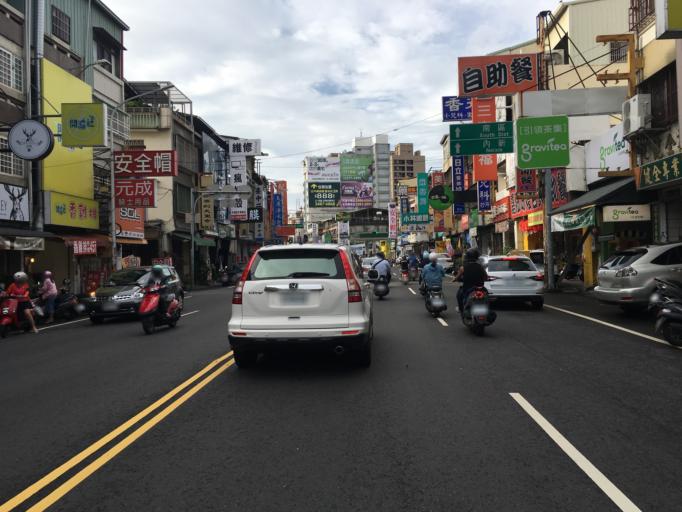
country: TW
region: Taiwan
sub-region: Taichung City
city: Taichung
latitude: 24.1068
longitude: 120.6897
